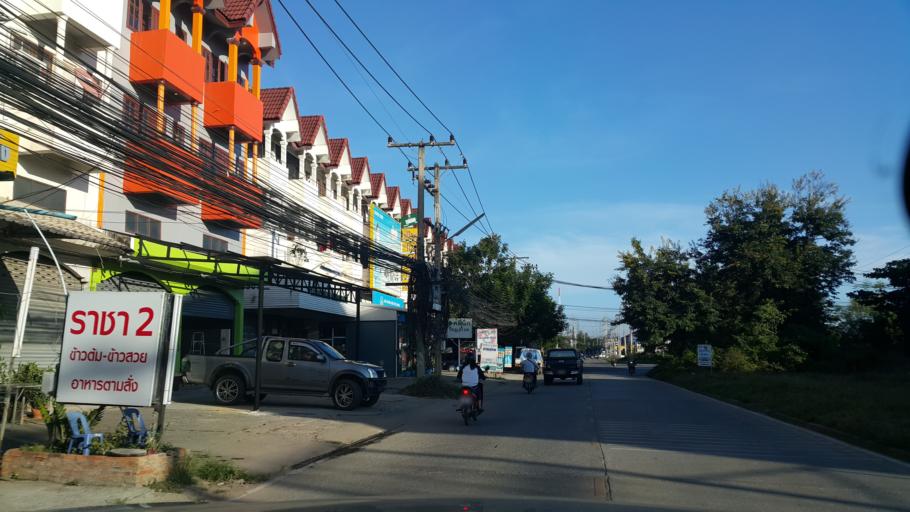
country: TH
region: Lamphun
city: Lamphun
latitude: 18.5928
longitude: 99.0364
